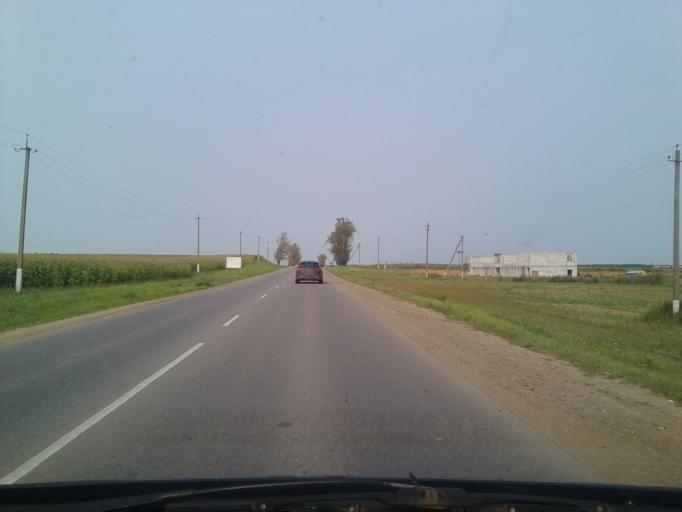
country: BY
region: Minsk
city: Hatava
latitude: 53.7860
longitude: 27.6532
